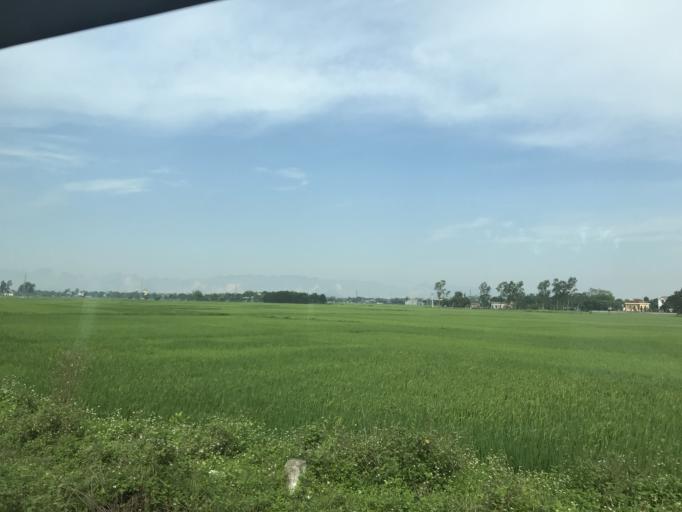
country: VN
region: Ha Nam
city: Thanh Pho Phu Ly
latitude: 20.5180
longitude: 105.9431
